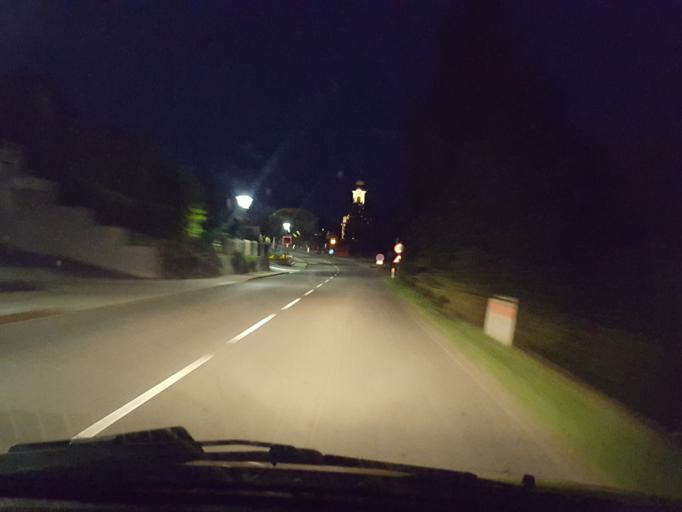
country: AT
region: Lower Austria
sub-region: Politischer Bezirk Scheibbs
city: Sankt Georgen an der Leys
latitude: 48.0307
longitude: 15.2229
